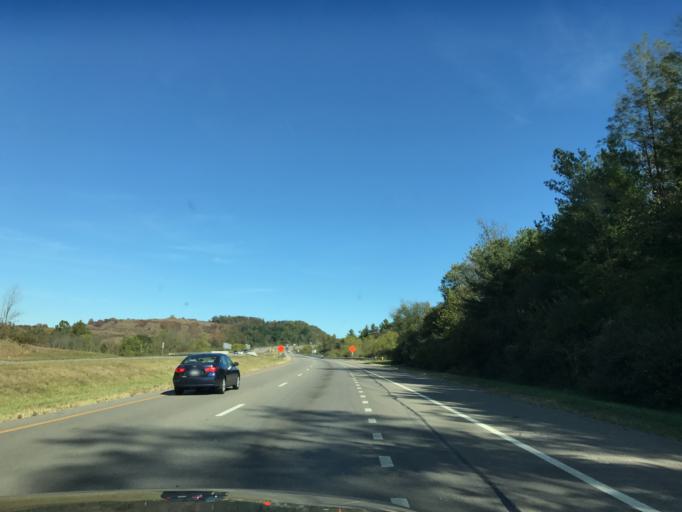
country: US
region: Ohio
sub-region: Belmont County
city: Barnesville
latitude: 40.0578
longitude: -81.1512
